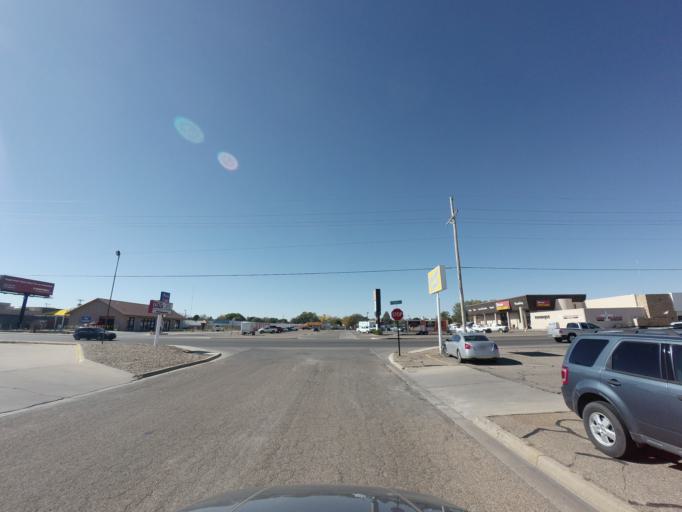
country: US
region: New Mexico
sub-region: Curry County
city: Clovis
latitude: 34.4216
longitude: -103.1961
